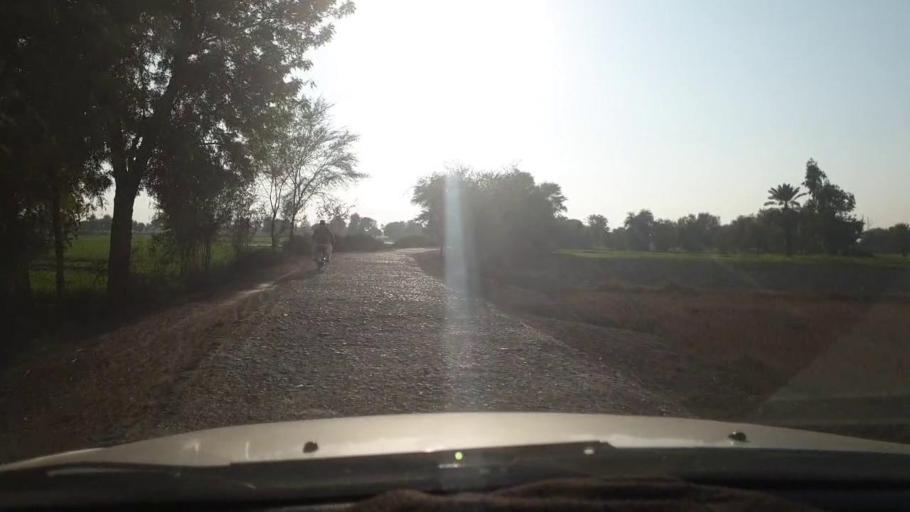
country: PK
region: Sindh
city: Mirpur Mathelo
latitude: 27.9980
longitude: 69.5231
